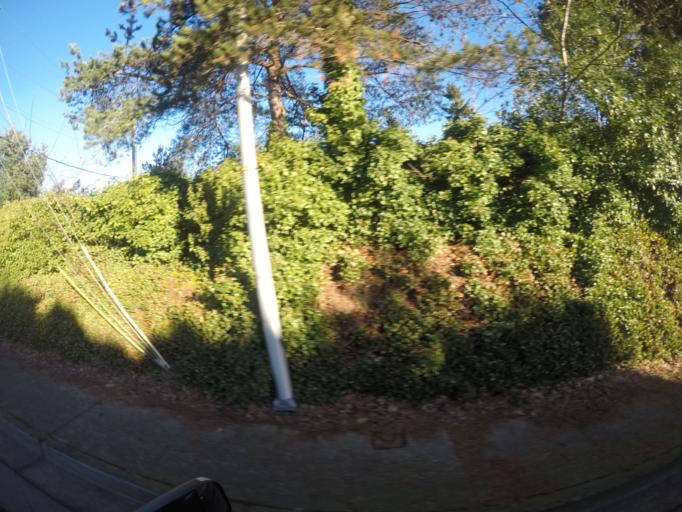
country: US
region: Washington
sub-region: Clark County
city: Walnut Grove
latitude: 45.6144
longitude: -122.5855
